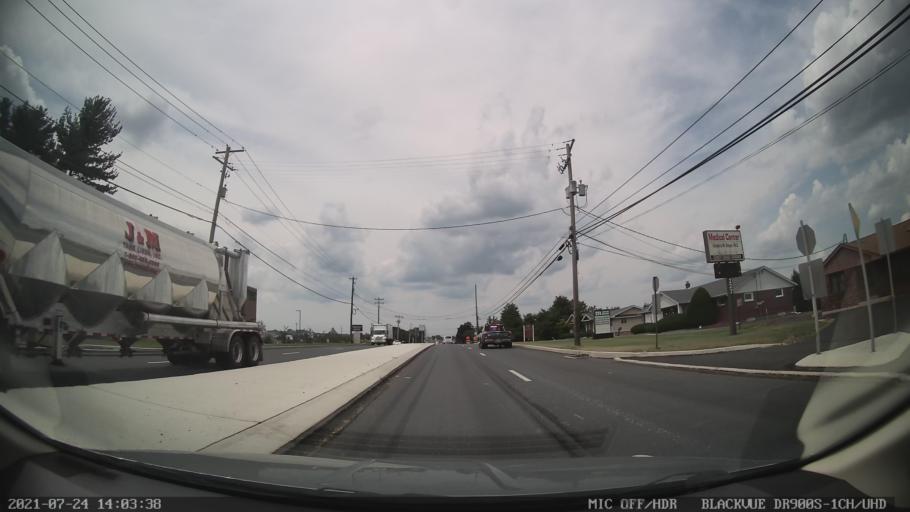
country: US
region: Pennsylvania
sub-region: Lehigh County
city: Trexlertown
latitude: 40.5685
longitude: -75.6154
